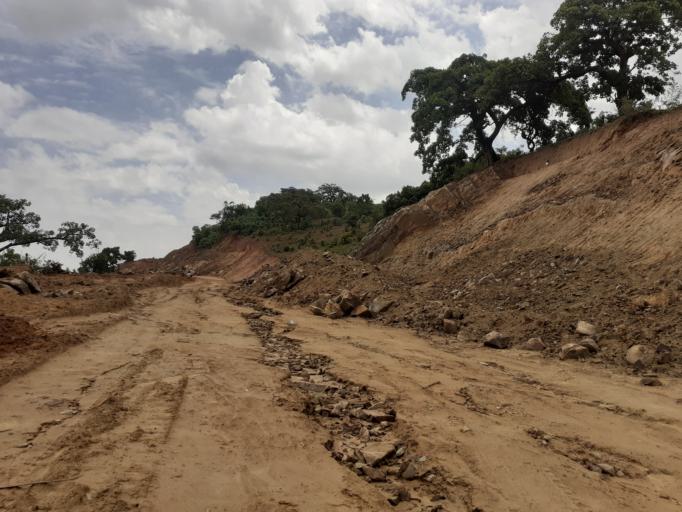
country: ET
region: Oromiya
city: Gimbi
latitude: 9.3236
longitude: 35.6919
